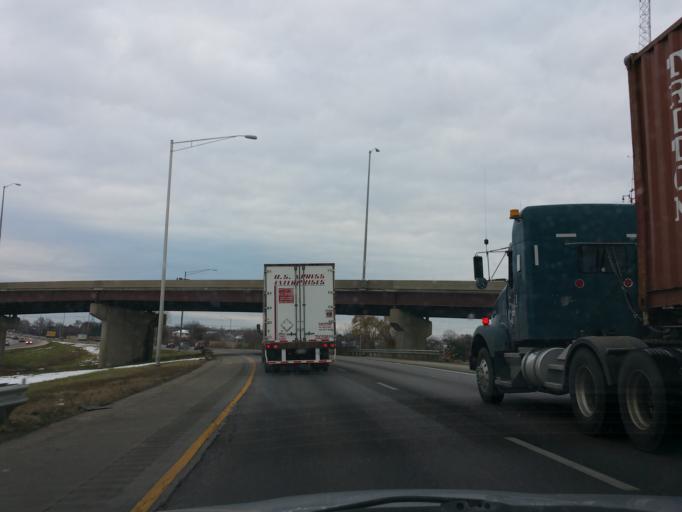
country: US
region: Illinois
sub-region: DuPage County
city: Itasca
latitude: 41.9592
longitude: -88.0258
